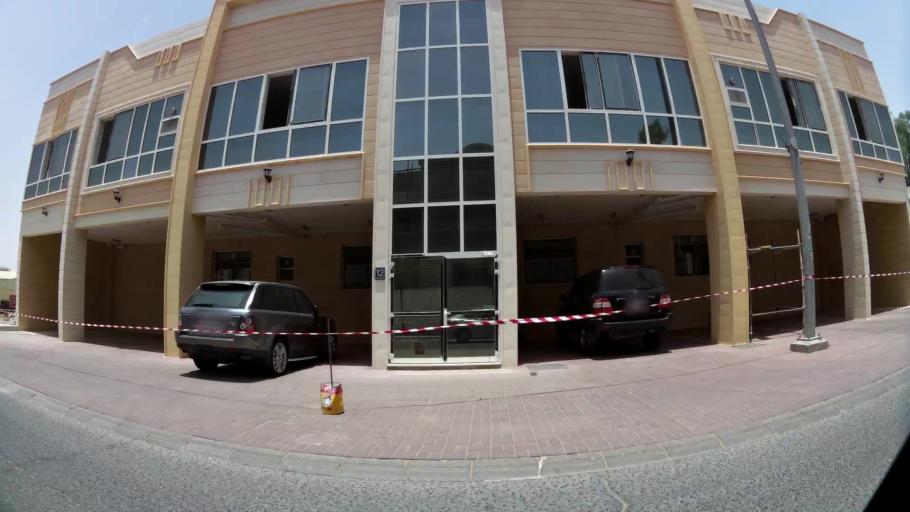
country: AE
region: Abu Dhabi
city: Al Ain
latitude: 24.2110
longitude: 55.7545
